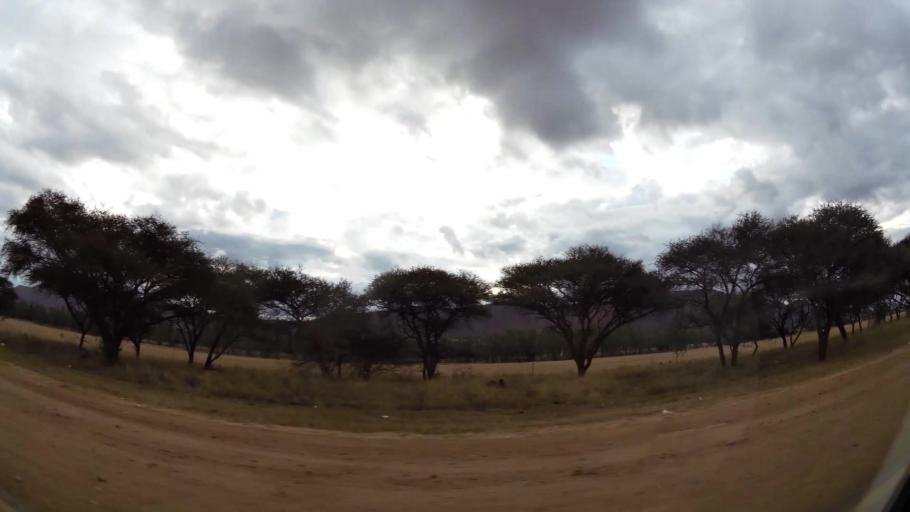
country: ZA
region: Limpopo
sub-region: Waterberg District Municipality
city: Mokopane
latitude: -24.2694
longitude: 28.9818
